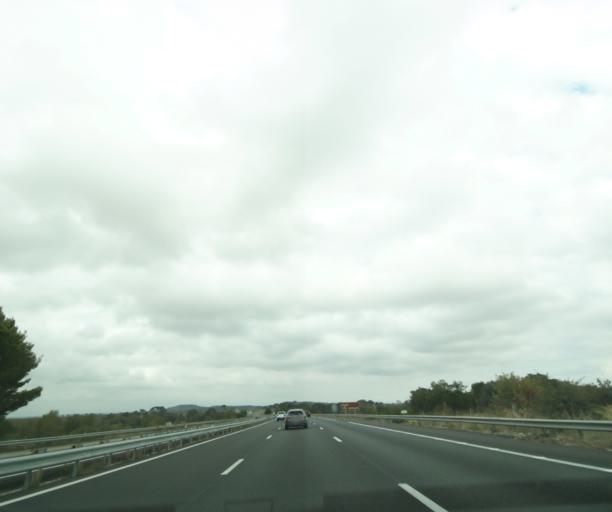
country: FR
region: Languedoc-Roussillon
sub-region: Departement de l'Herault
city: Montblanc
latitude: 43.3645
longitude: 3.3821
